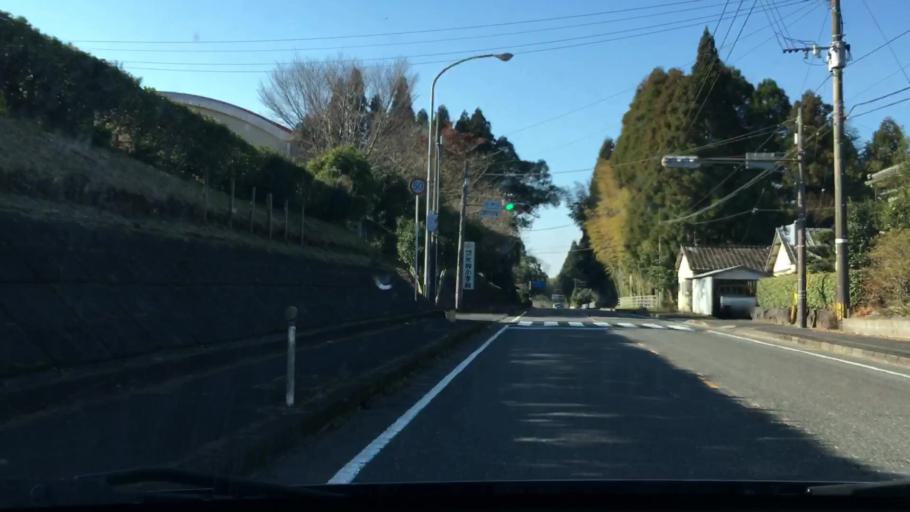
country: JP
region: Kagoshima
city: Sueyoshicho-ninokata
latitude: 31.6768
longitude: 130.9292
